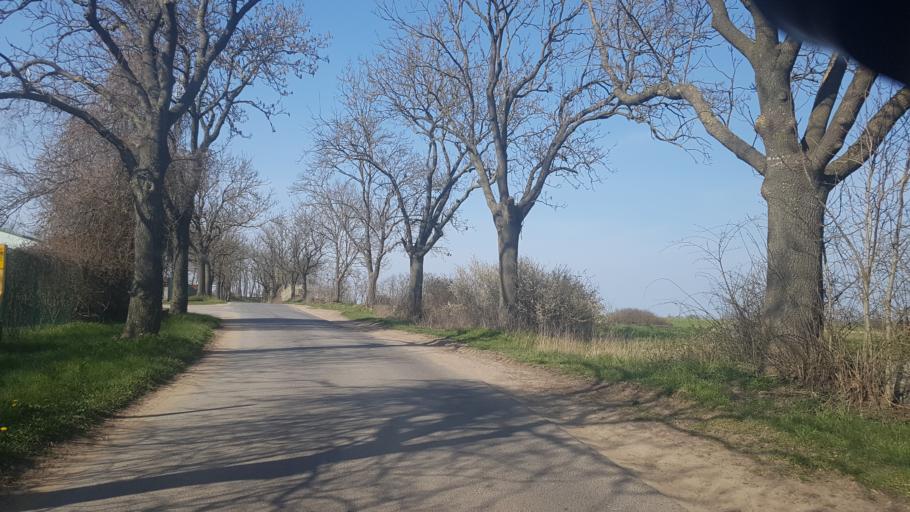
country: DE
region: Brandenburg
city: Gerswalde
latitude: 53.1895
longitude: 13.7796
